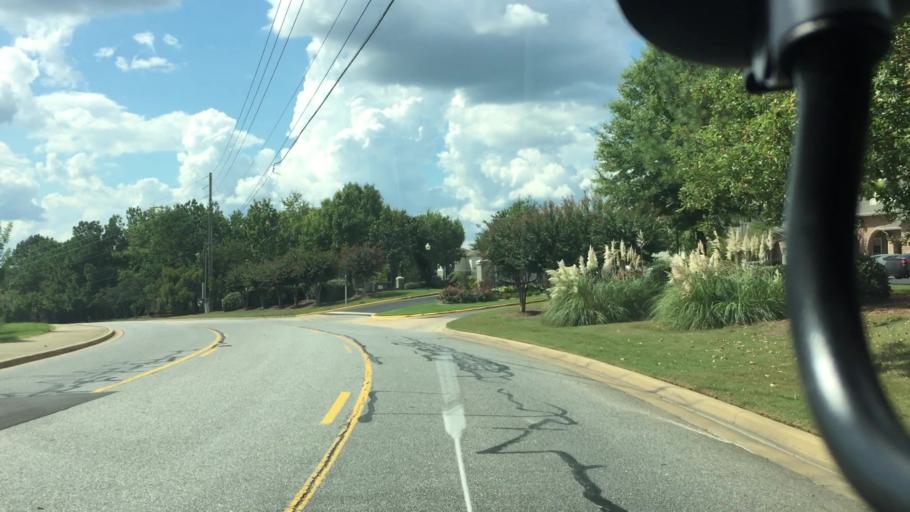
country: US
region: Alabama
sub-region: Lee County
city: Auburn
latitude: 32.5744
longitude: -85.5029
